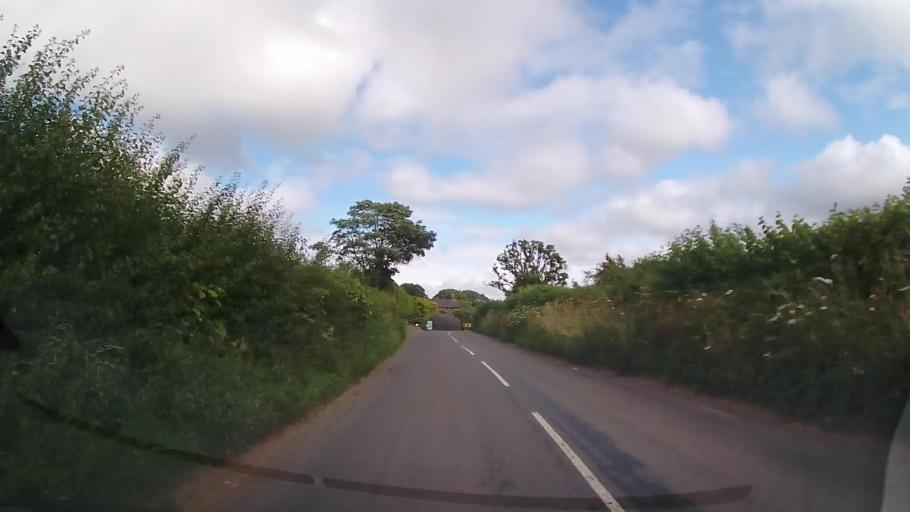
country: GB
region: England
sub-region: Shropshire
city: Great Ness
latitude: 52.7993
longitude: -2.9398
